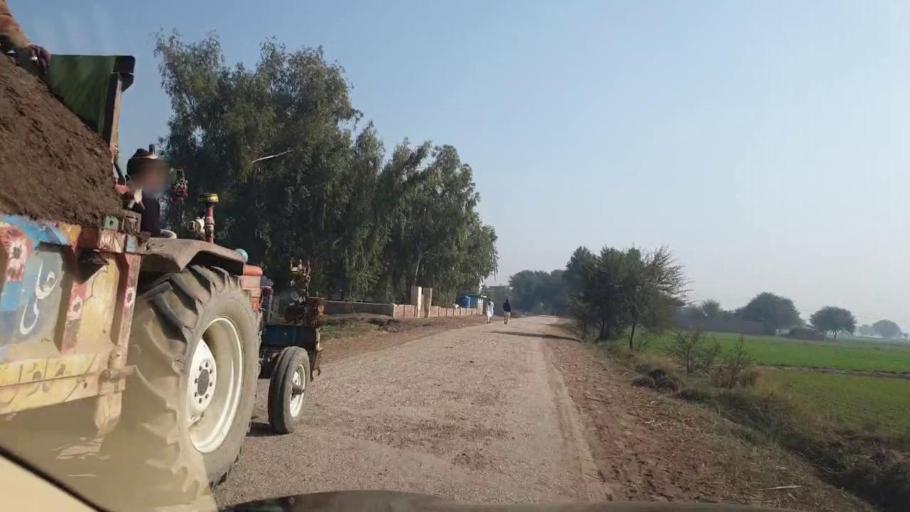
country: PK
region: Sindh
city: Ubauro
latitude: 28.1141
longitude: 69.7265
